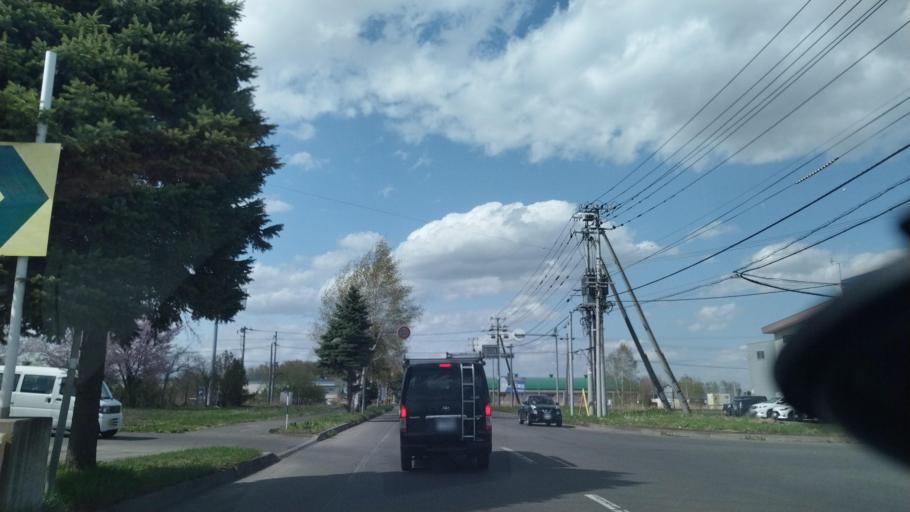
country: JP
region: Hokkaido
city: Obihiro
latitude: 42.9242
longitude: 143.1436
